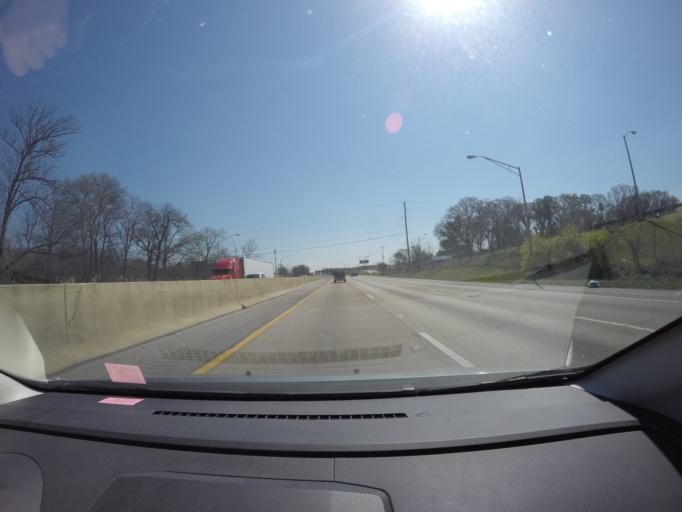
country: US
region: Tennessee
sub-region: Hamilton County
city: East Ridge
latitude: 35.0063
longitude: -85.2312
